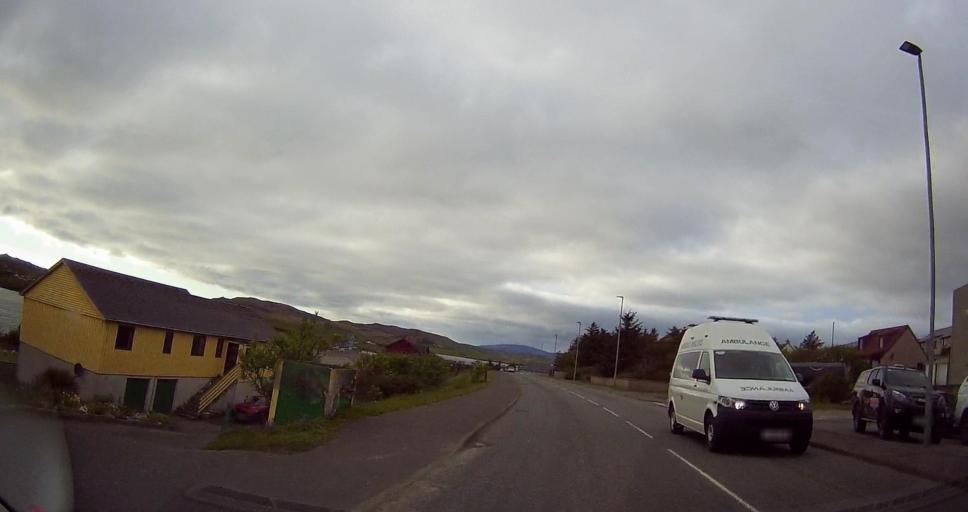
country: GB
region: Scotland
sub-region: Shetland Islands
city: Lerwick
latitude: 60.3915
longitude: -1.3495
